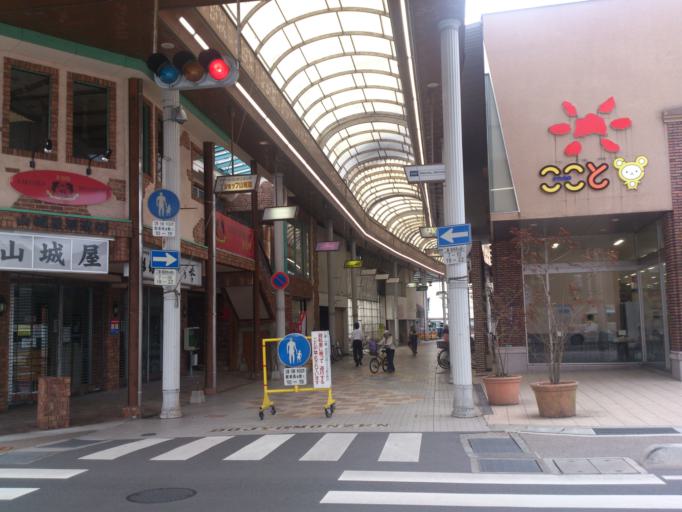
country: JP
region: Yamaguchi
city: Yamaguchi-shi
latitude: 34.1747
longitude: 131.4754
